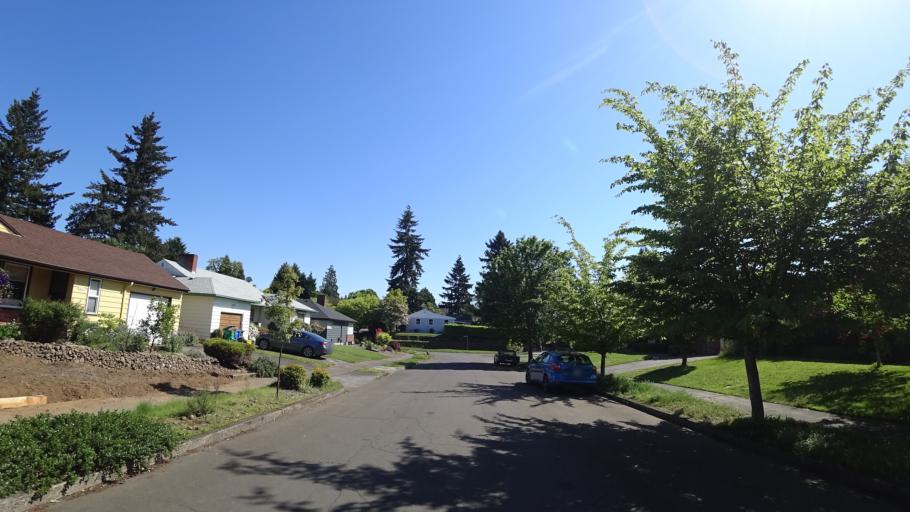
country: US
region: Oregon
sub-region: Clackamas County
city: Milwaukie
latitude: 45.4833
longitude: -122.6188
